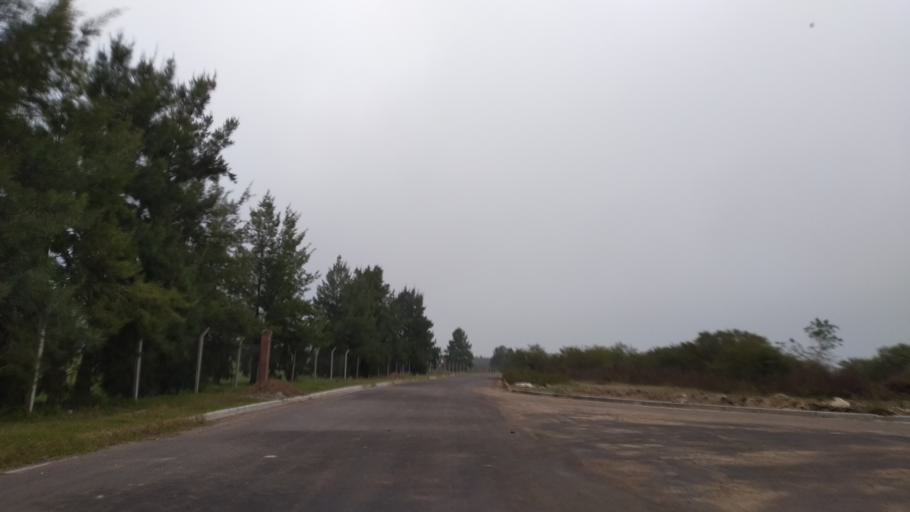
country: AR
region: Santa Fe
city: Funes
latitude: -32.9373
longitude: -60.7676
